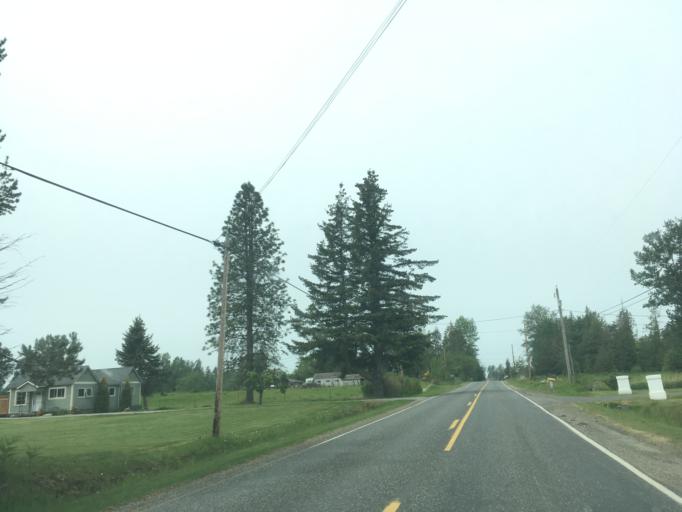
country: US
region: Washington
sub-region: Whatcom County
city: Bellingham
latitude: 48.8188
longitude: -122.4484
